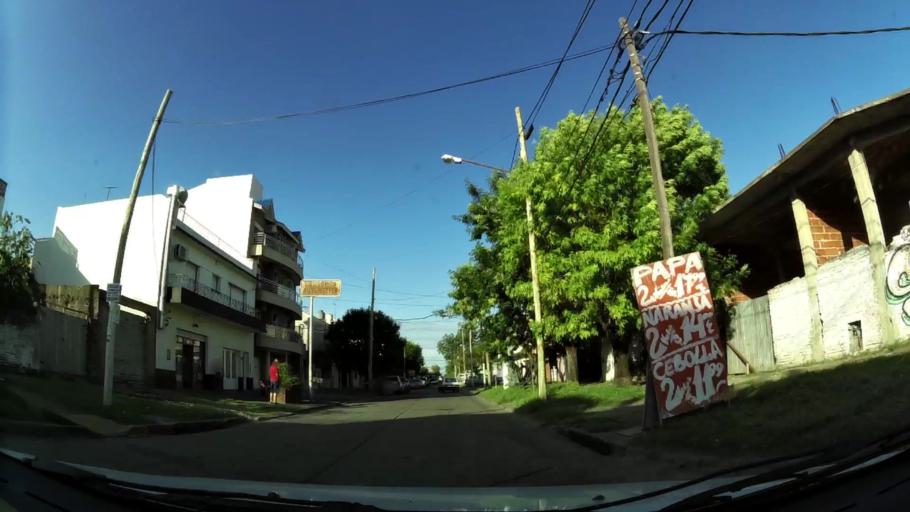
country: AR
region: Buenos Aires
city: Caseros
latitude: -34.5831
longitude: -58.5828
